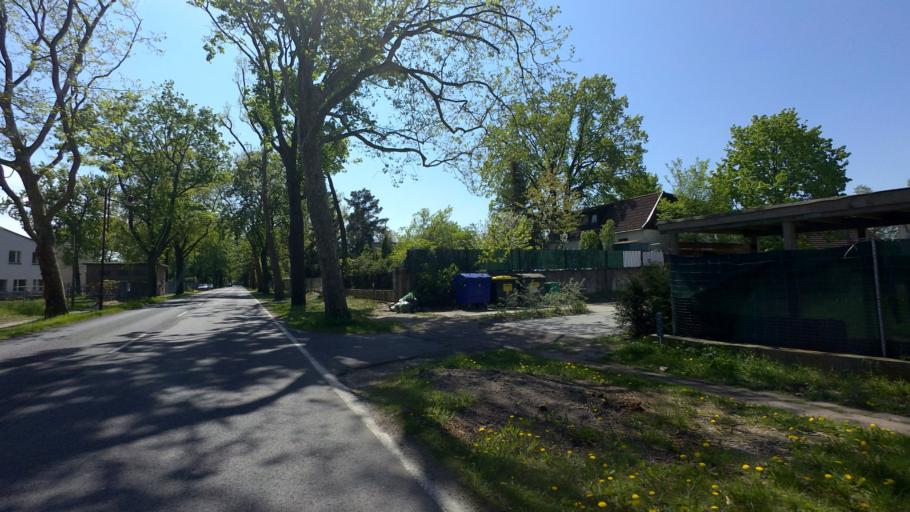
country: DE
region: Brandenburg
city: Bestensee
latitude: 52.2351
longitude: 13.6673
